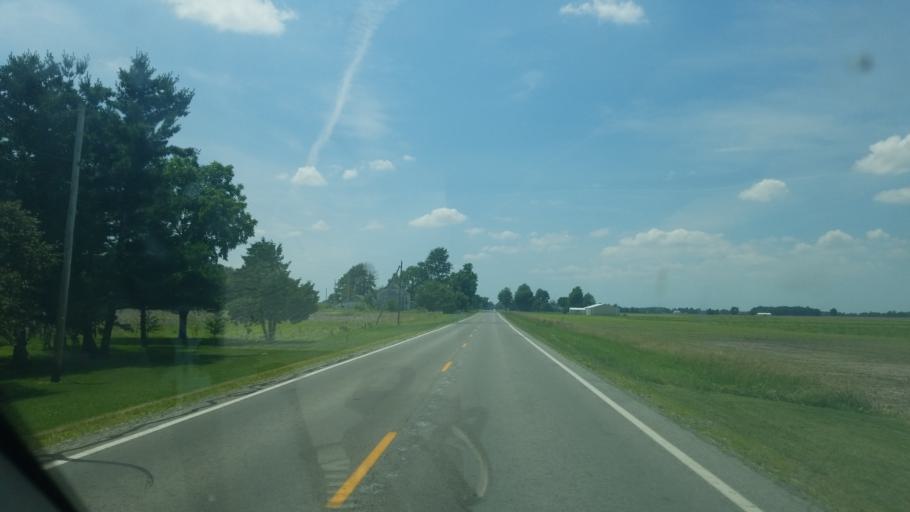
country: US
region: Ohio
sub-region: Hardin County
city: Ada
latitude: 40.7766
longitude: -83.7875
